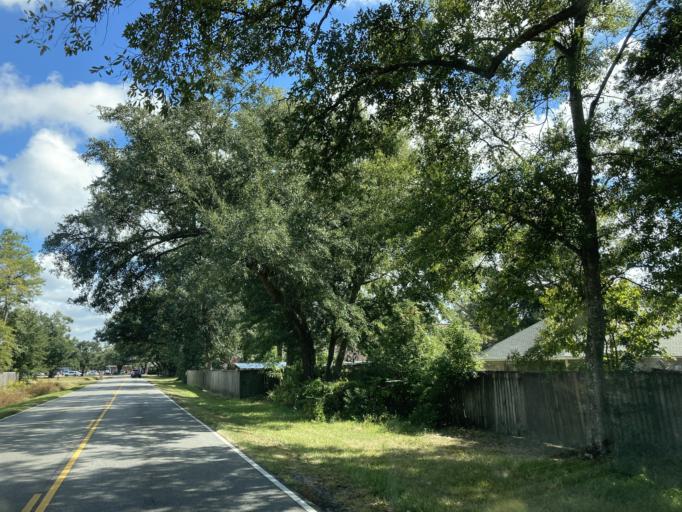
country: US
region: Mississippi
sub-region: Jackson County
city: Gulf Hills
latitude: 30.4510
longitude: -88.8326
